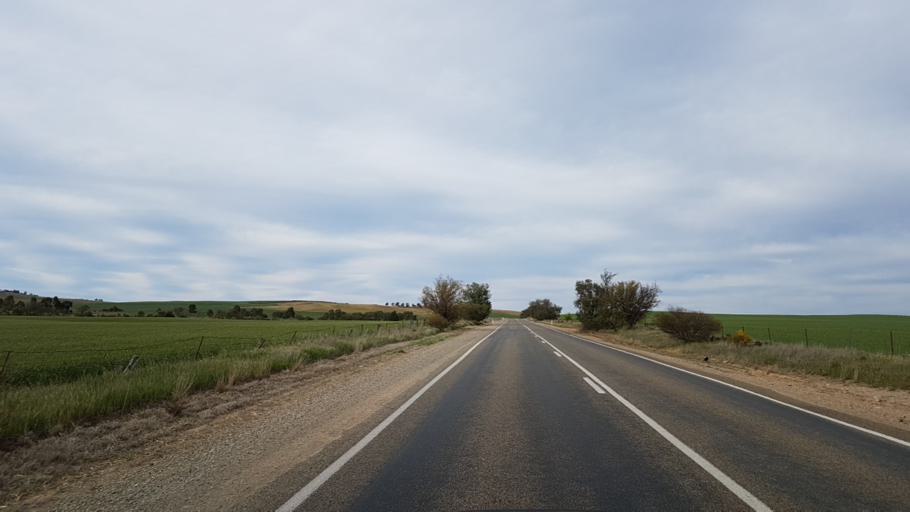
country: AU
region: South Australia
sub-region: Northern Areas
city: Jamestown
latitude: -33.2108
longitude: 138.4246
